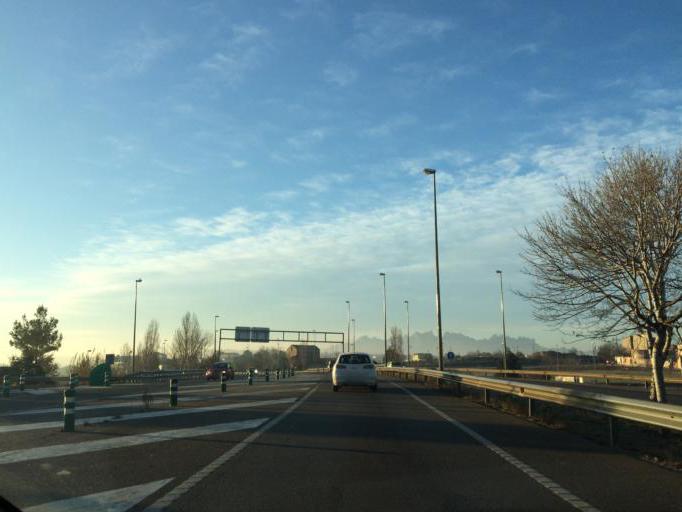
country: ES
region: Catalonia
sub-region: Provincia de Barcelona
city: Sant Fruitos de Bages
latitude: 41.7378
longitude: 1.8496
